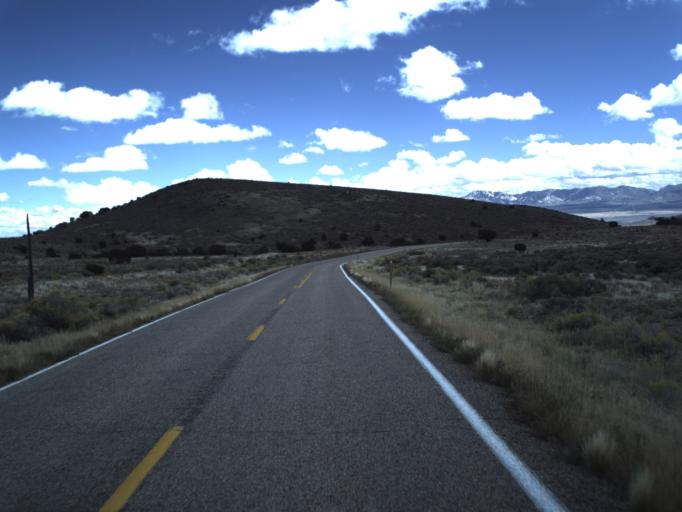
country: US
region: Utah
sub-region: Beaver County
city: Milford
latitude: 38.4612
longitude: -113.2379
